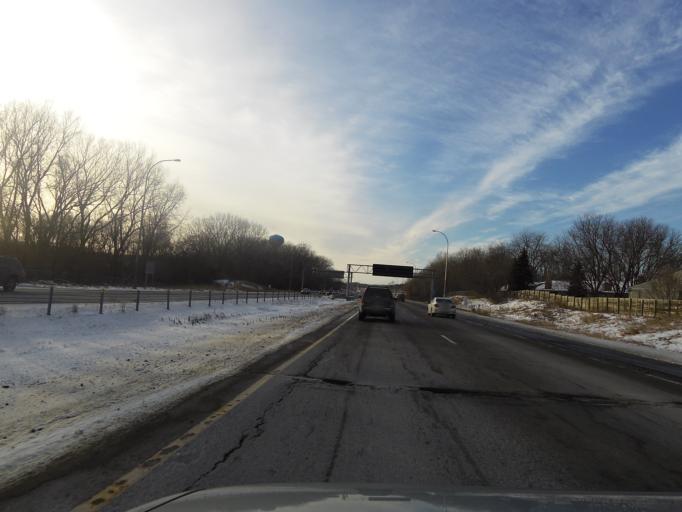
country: US
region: Minnesota
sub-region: Hennepin County
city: Edina
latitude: 44.8884
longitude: -93.3762
